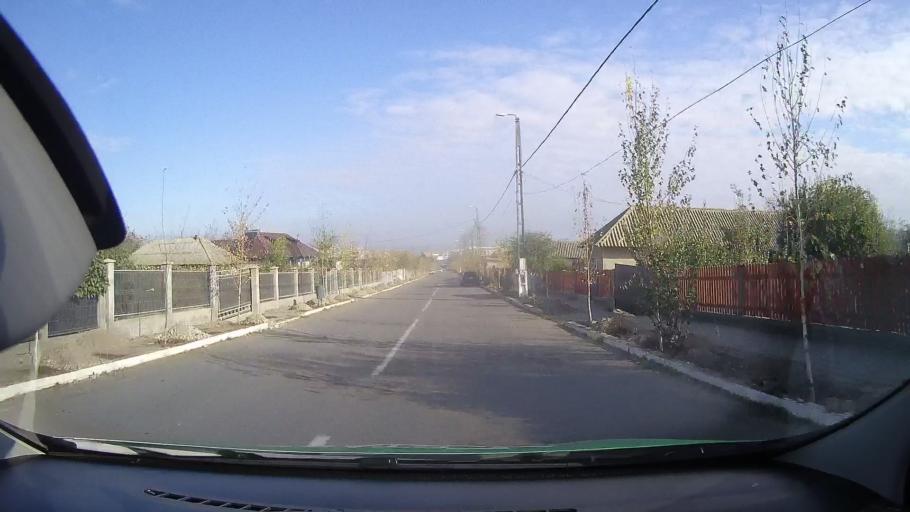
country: RO
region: Tulcea
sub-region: Comuna Mahmudia
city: Mahmudia
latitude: 45.0843
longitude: 29.0838
